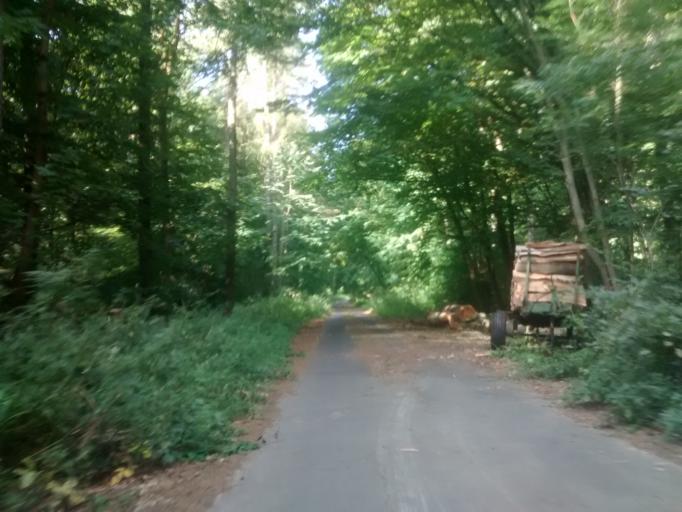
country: DE
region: Hesse
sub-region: Regierungsbezirk Giessen
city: Colbe
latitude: 50.8094
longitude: 8.8210
